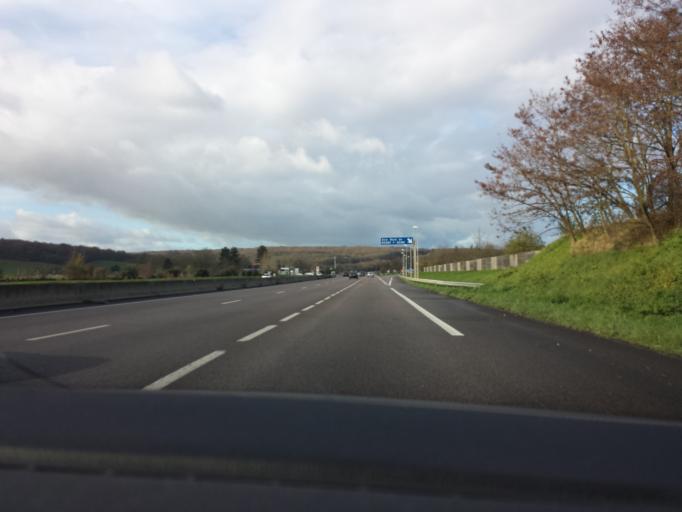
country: FR
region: Ile-de-France
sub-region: Departement des Yvelines
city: Rosny-sur-Seine
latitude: 48.9917
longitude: 1.6395
